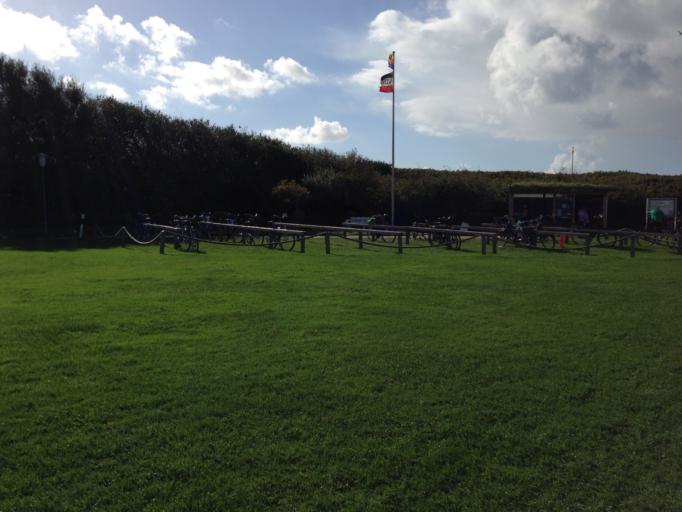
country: DE
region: Schleswig-Holstein
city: Utersum
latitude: 54.7136
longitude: 8.3977
